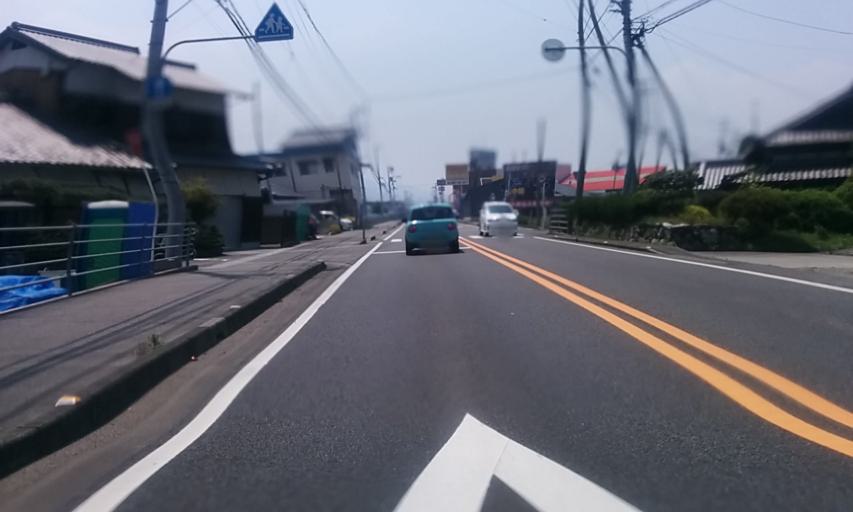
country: JP
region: Ehime
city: Saijo
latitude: 33.9097
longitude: 133.1950
